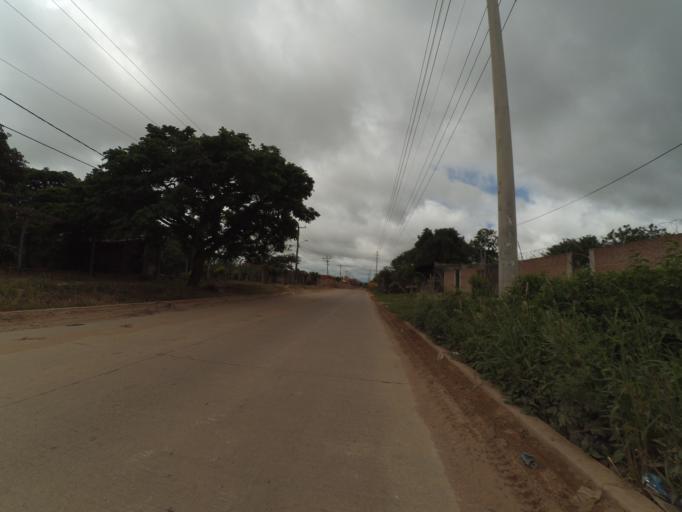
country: BO
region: Santa Cruz
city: Santa Cruz de la Sierra
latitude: -17.8612
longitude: -63.2260
